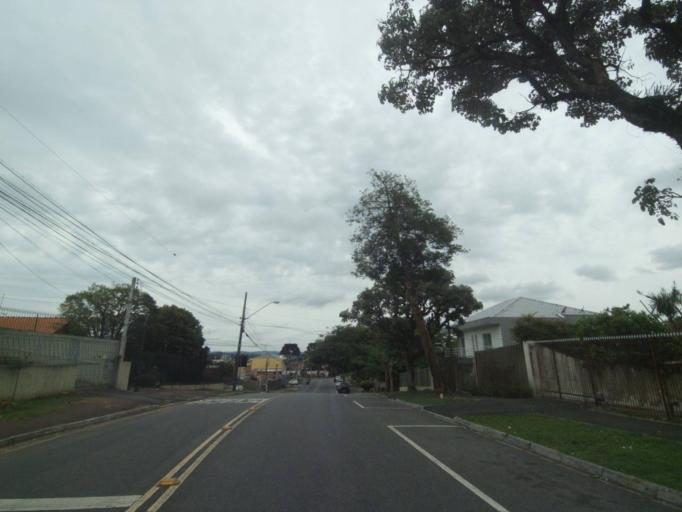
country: BR
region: Parana
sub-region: Curitiba
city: Curitiba
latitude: -25.3949
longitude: -49.2944
